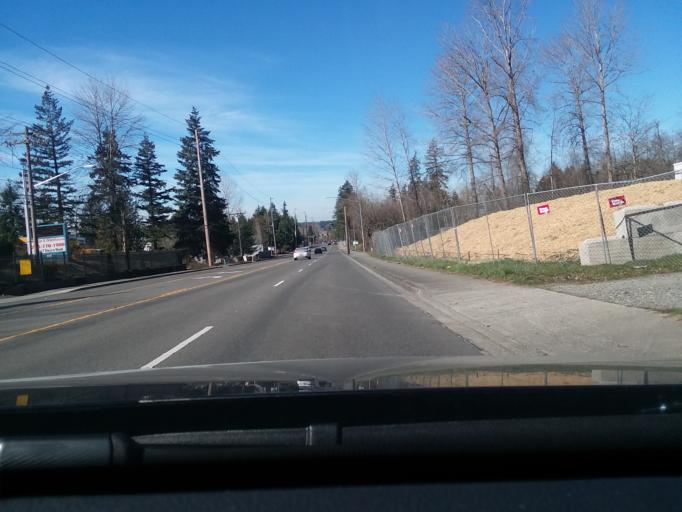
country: US
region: Washington
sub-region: Pierce County
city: South Hill
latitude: 47.1547
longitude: -122.2763
